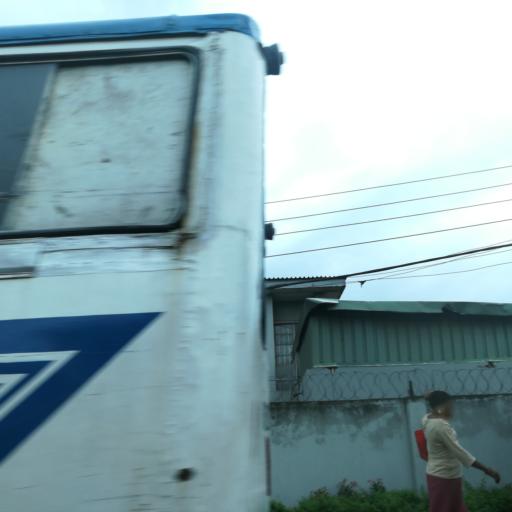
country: NG
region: Lagos
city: Oshodi
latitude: 6.5547
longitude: 3.3472
